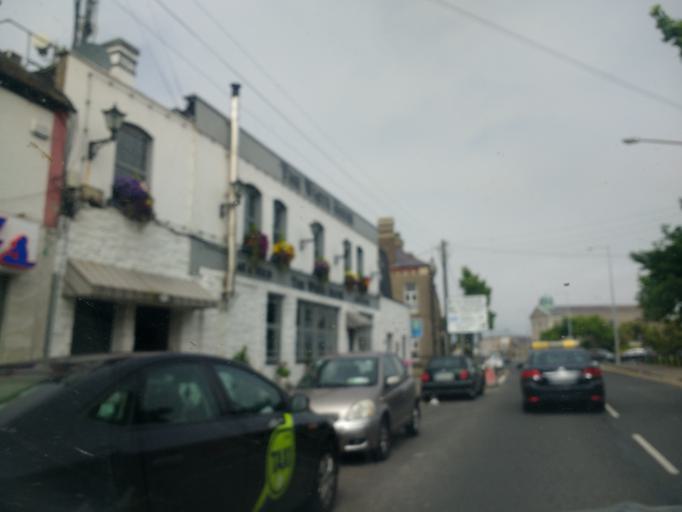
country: IE
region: Leinster
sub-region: Fingal County
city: Baldoyle
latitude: 53.3979
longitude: -6.1269
